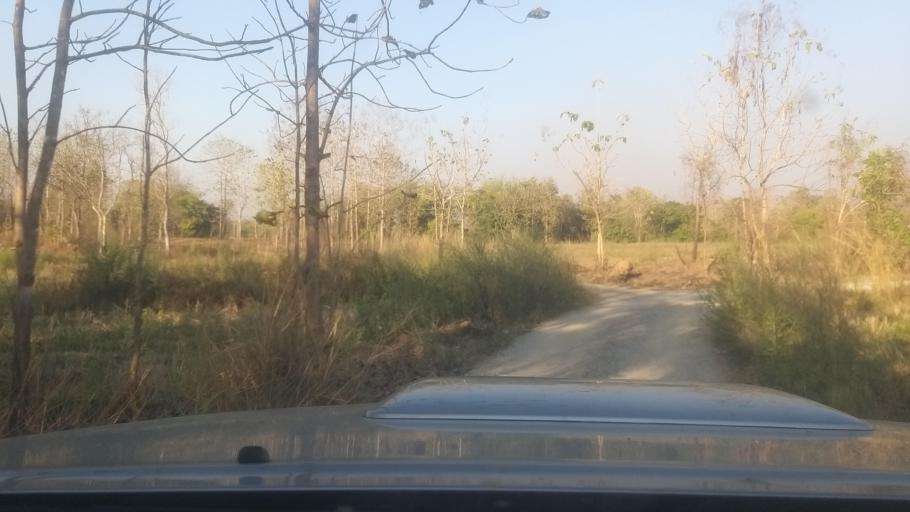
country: TH
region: Phrae
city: Nong Muang Khai
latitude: 18.2681
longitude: 100.0232
